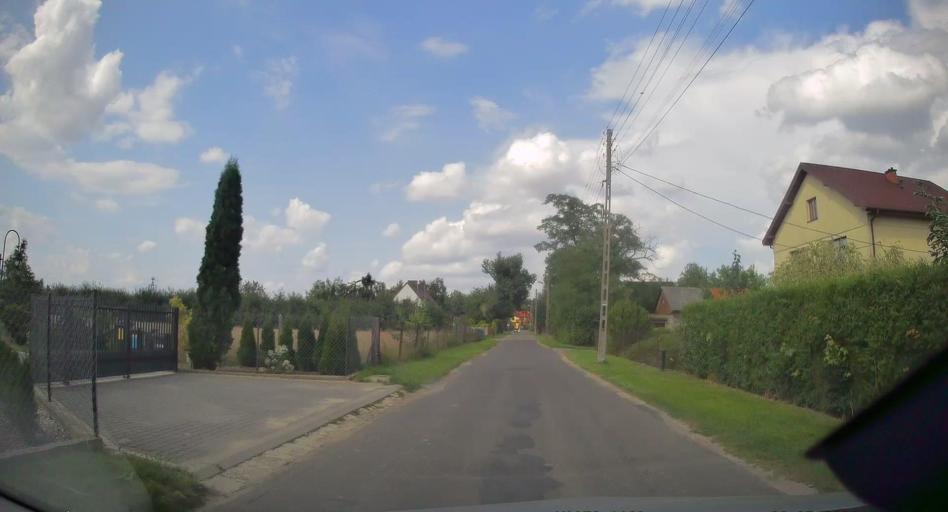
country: PL
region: Lodz Voivodeship
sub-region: Powiat brzezinski
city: Rogow
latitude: 51.8197
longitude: 19.8981
